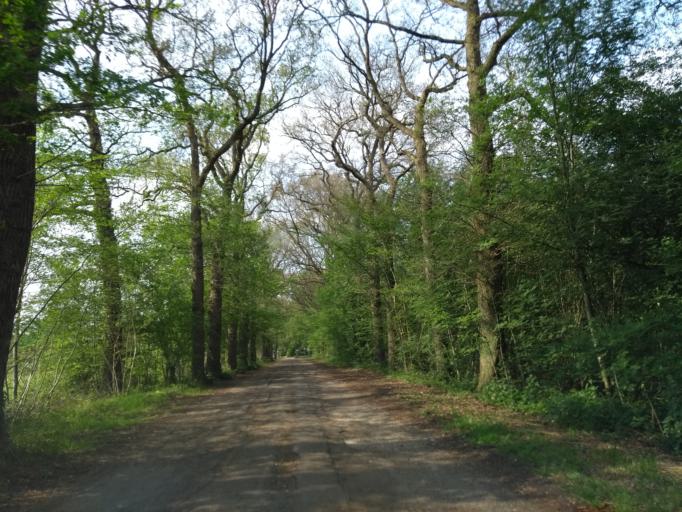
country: NL
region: Overijssel
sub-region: Gemeente Staphorst
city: Staphorst
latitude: 52.6720
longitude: 6.2732
